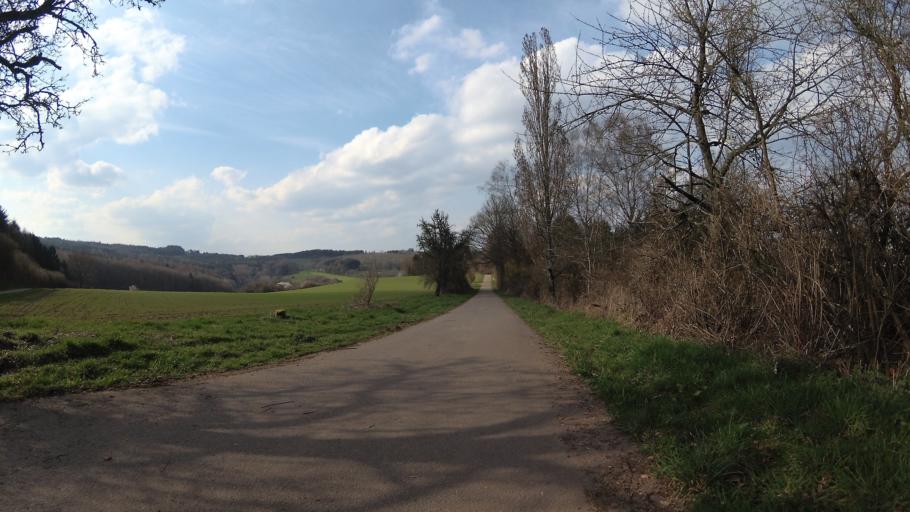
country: DE
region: Saarland
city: Ottweiler
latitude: 49.4004
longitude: 7.1424
